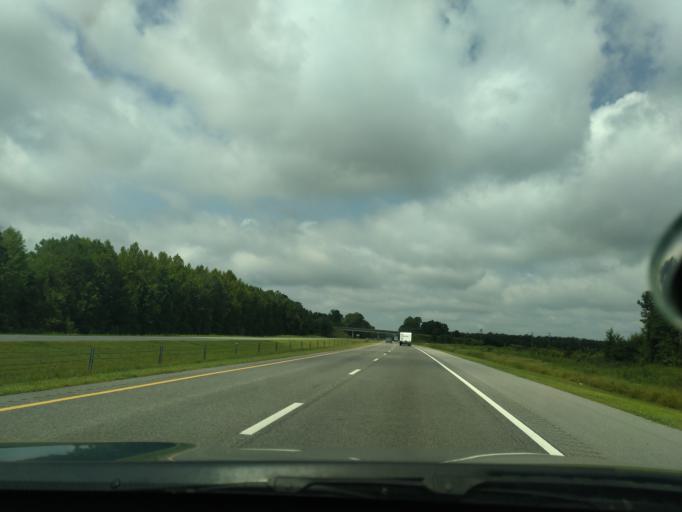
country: US
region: North Carolina
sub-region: Martin County
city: Robersonville
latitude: 35.8337
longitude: -77.3141
